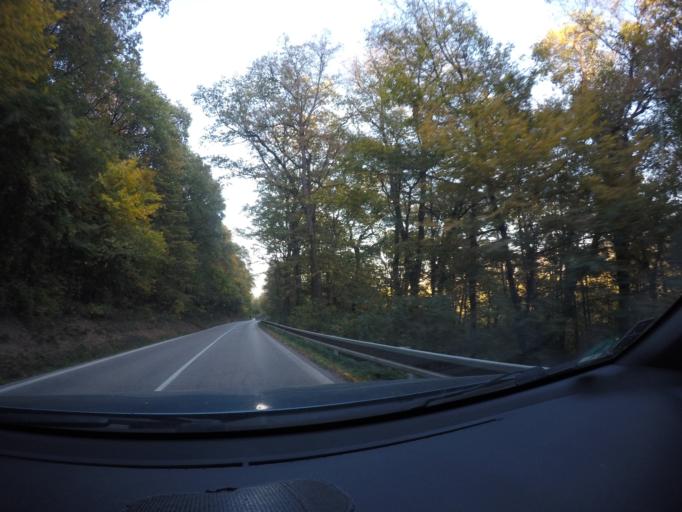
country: SK
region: Trenciansky
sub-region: Okres Trencin
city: Trencin
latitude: 48.9077
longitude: 18.0739
